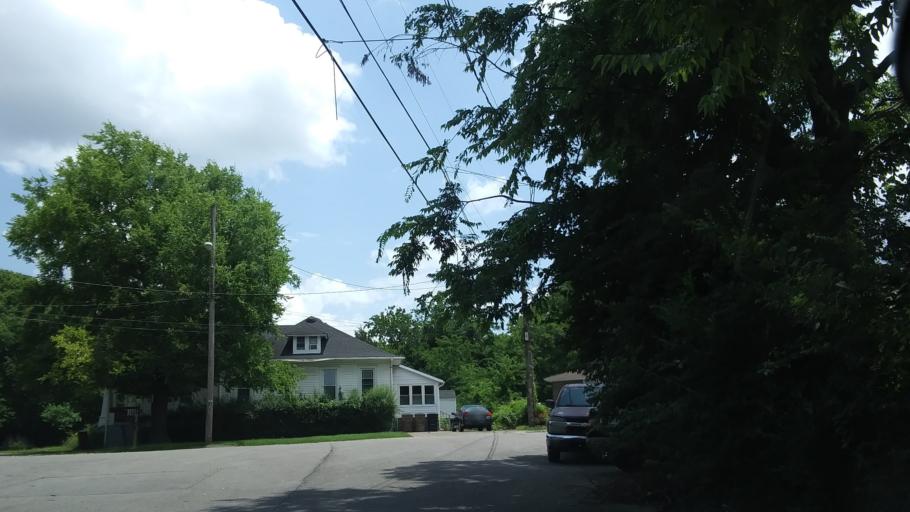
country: US
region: Tennessee
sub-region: Davidson County
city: Belle Meade
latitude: 36.1576
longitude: -86.8787
